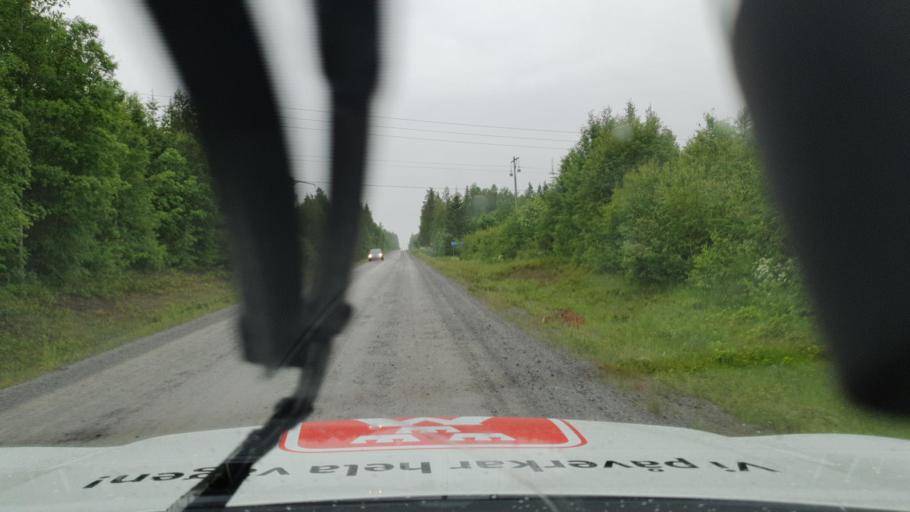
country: SE
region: Vaesterbotten
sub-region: Bjurholms Kommun
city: Bjurholm
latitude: 63.8553
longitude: 19.4721
